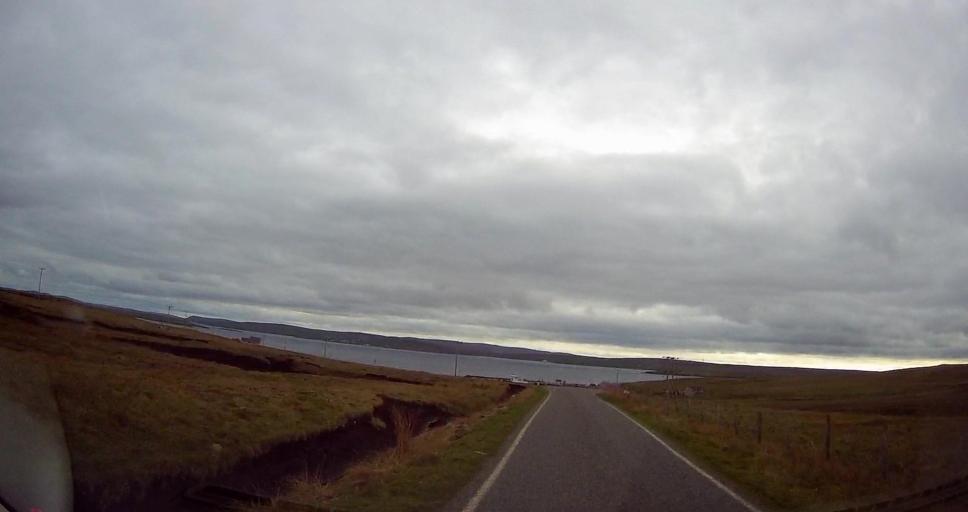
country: GB
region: Scotland
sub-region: Shetland Islands
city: Shetland
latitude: 60.5012
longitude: -1.1510
